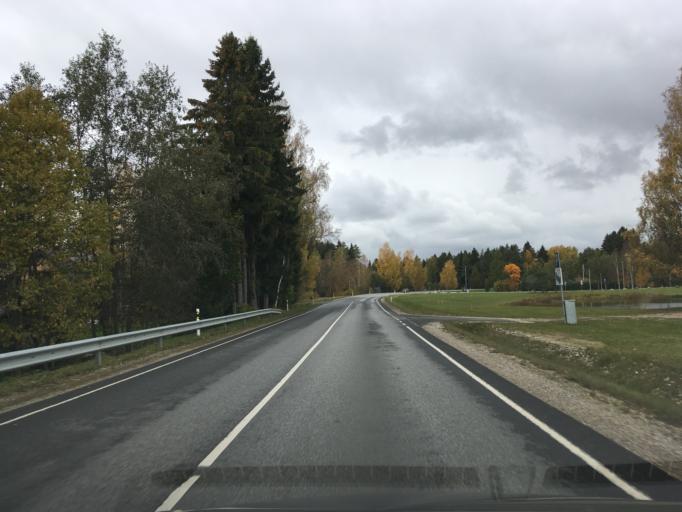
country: EE
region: Harju
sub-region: Anija vald
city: Kehra
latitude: 59.3109
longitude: 25.3466
